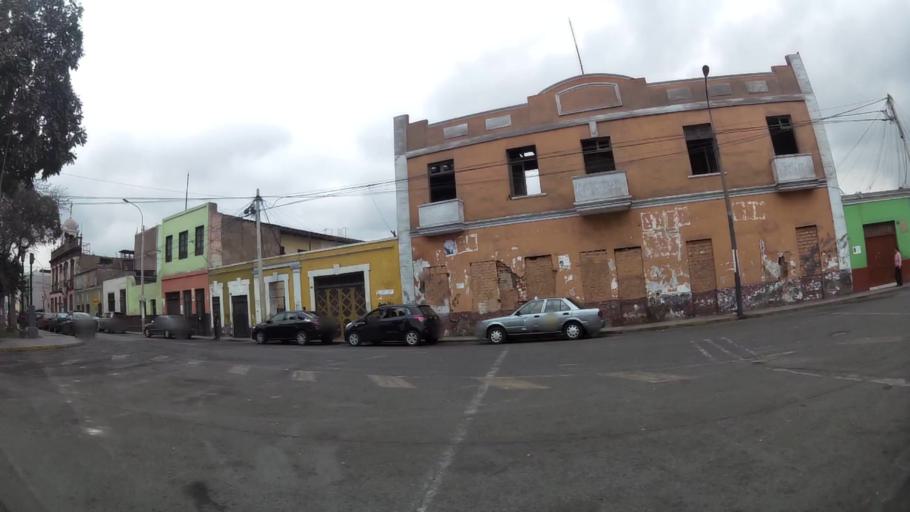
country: PE
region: Lima
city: Lima
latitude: -12.0407
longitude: -77.0399
